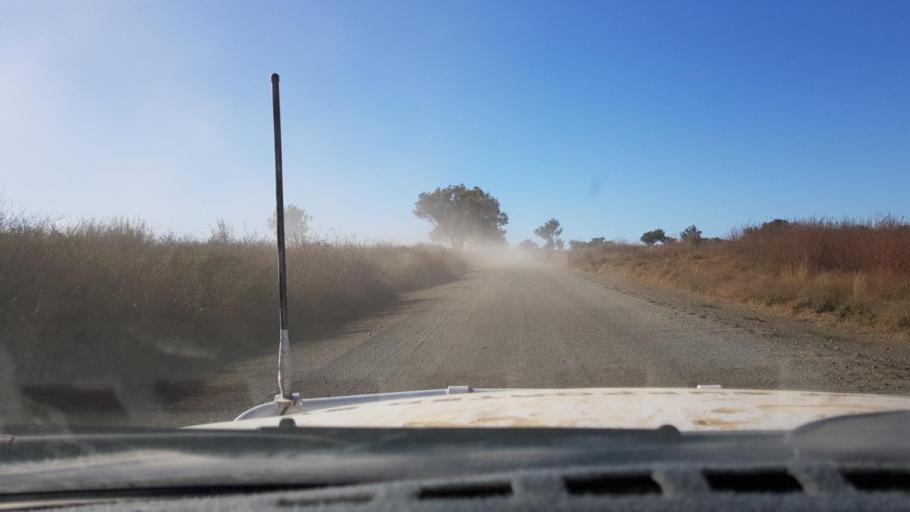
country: AU
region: New South Wales
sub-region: Narrabri
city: Blair Athol
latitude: -30.6686
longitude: 150.3741
